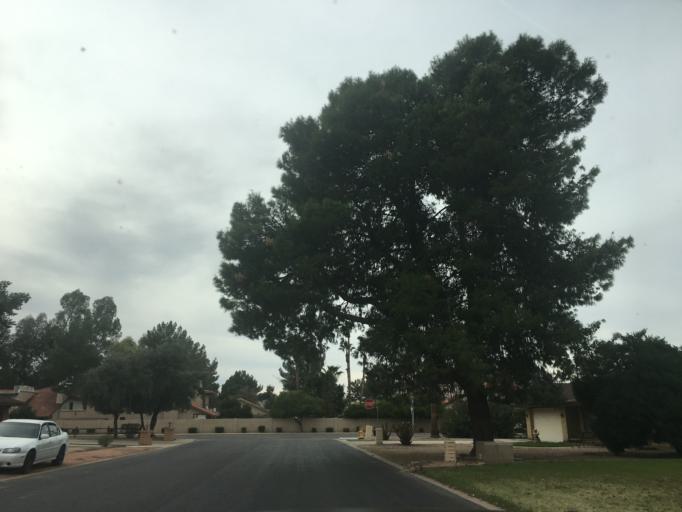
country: US
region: Arizona
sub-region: Maricopa County
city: Gilbert
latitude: 33.3631
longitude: -111.7814
